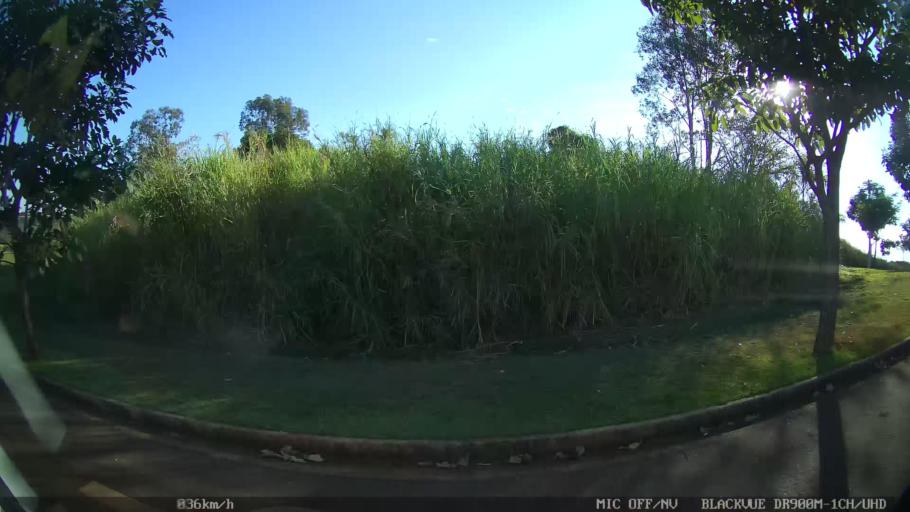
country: BR
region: Sao Paulo
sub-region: Piracicaba
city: Piracicaba
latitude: -22.6925
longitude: -47.6157
